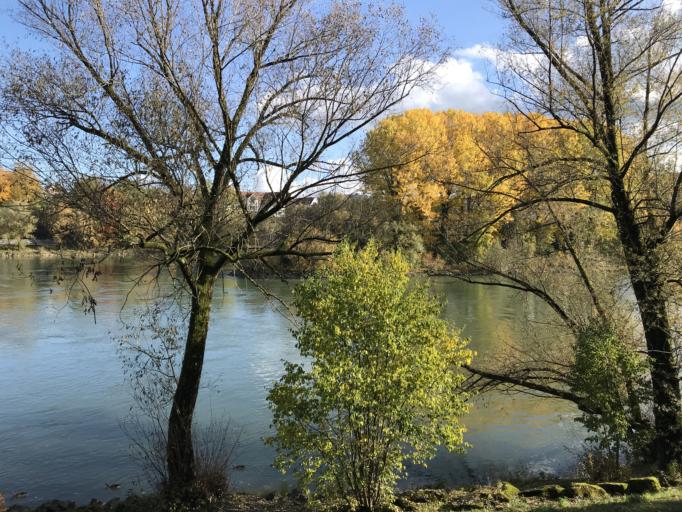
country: DE
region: Baden-Wuerttemberg
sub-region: Freiburg Region
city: Bad Sackingen
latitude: 47.5501
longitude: 7.9496
